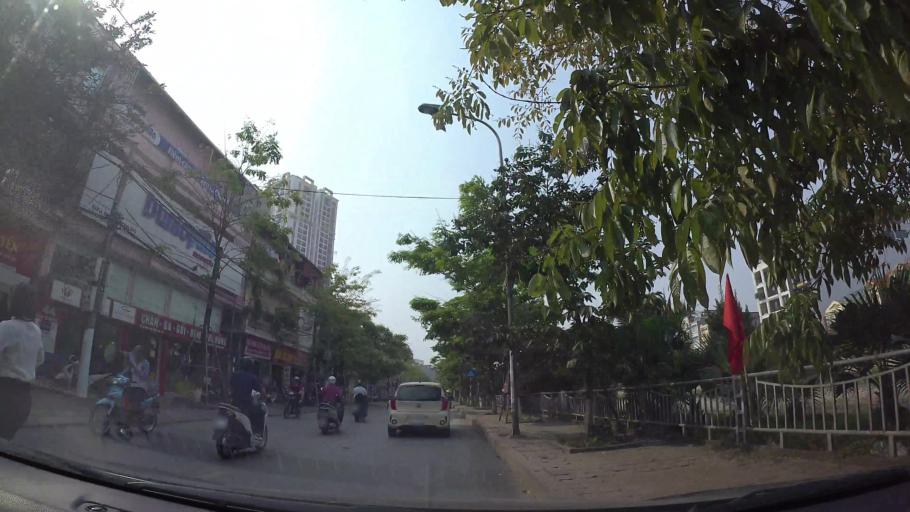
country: VN
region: Ha Noi
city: Thanh Xuan
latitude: 20.9844
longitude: 105.8146
